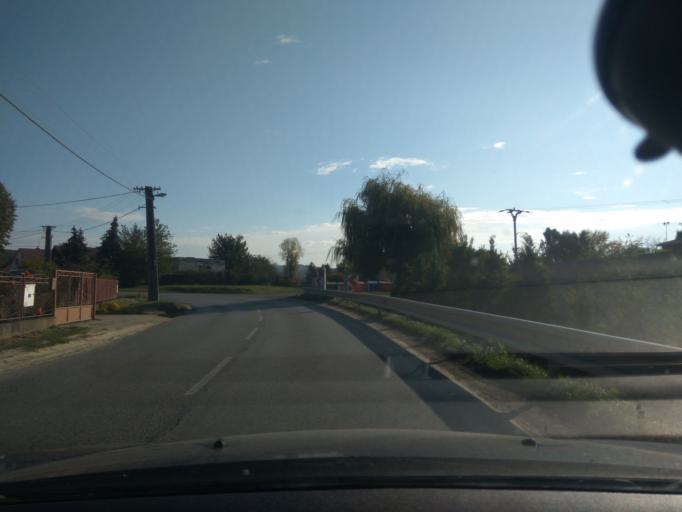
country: SK
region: Trnavsky
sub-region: Okres Trnava
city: Piestany
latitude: 48.5559
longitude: 17.8378
